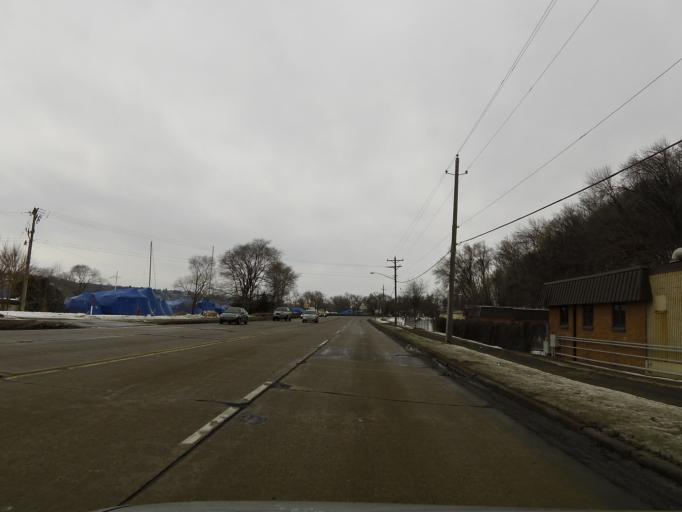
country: US
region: Wisconsin
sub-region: Saint Croix County
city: Hudson
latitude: 44.9669
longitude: -92.7554
